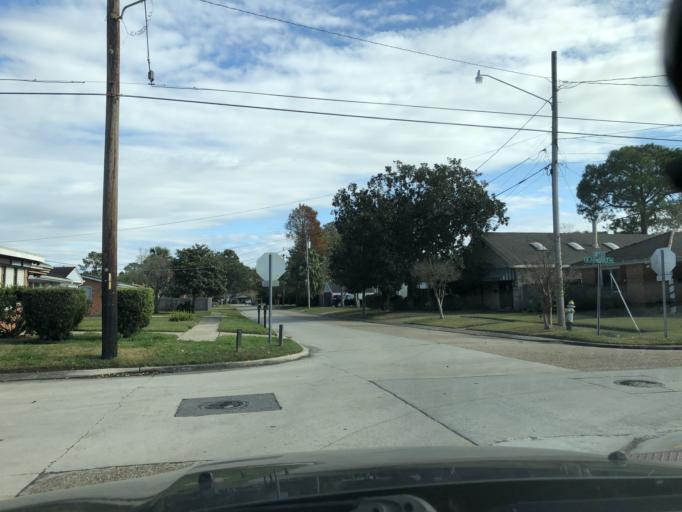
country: US
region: Louisiana
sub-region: Jefferson Parish
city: Metairie Terrace
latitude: 29.9847
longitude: -90.1616
